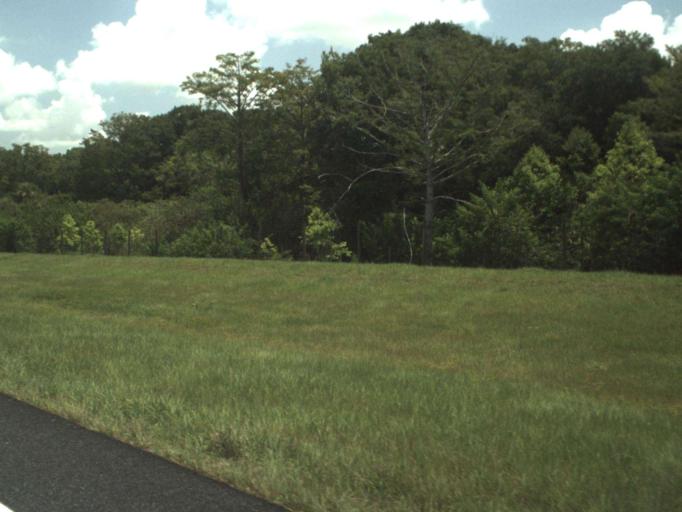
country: US
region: Florida
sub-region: Okeechobee County
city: Taylor Creek
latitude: 27.3206
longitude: -80.6547
